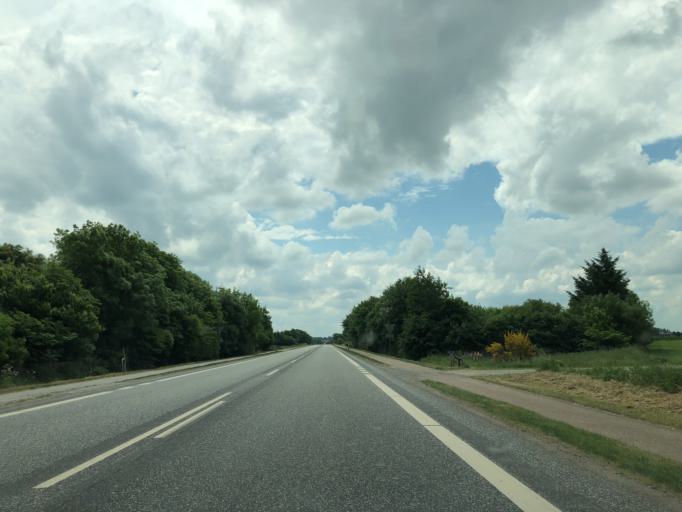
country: DK
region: Central Jutland
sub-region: Struer Kommune
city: Struer
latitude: 56.4707
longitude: 8.5867
